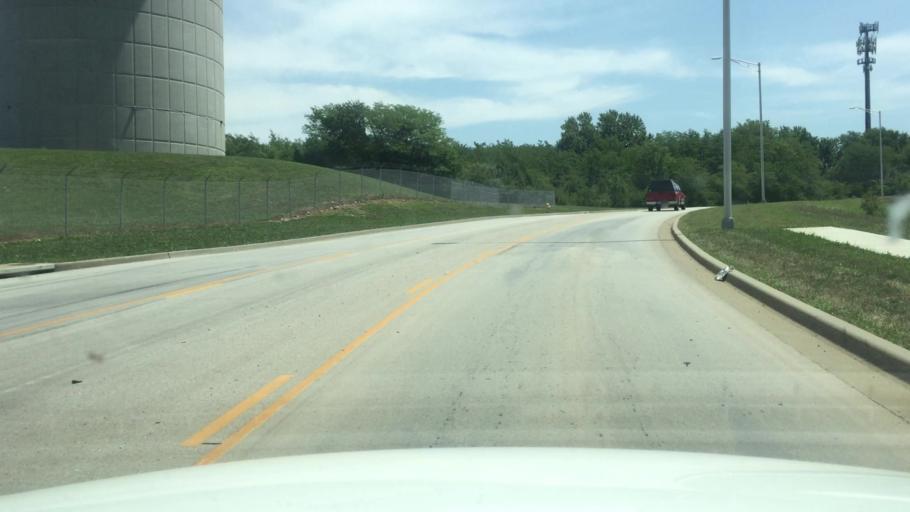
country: US
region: Missouri
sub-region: Jackson County
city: Blue Springs
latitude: 38.9851
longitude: -94.3520
